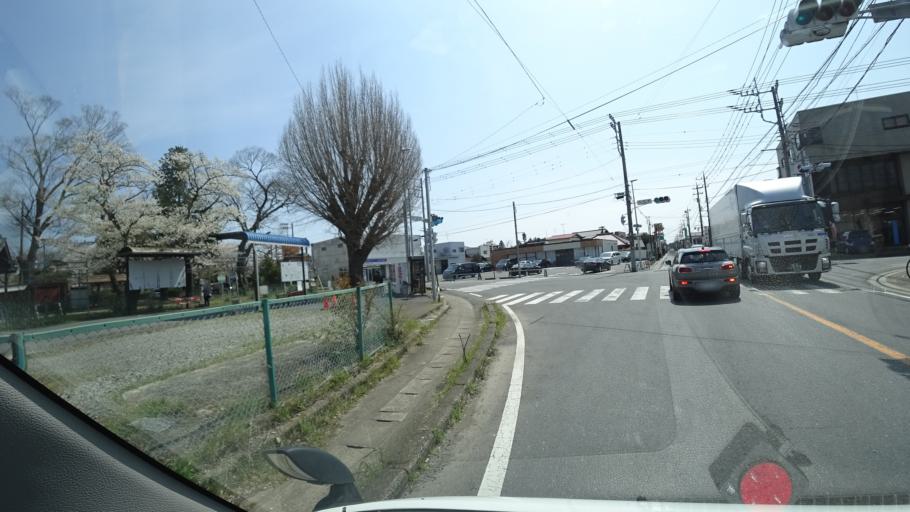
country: JP
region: Chiba
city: Narita
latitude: 35.7478
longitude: 140.3748
